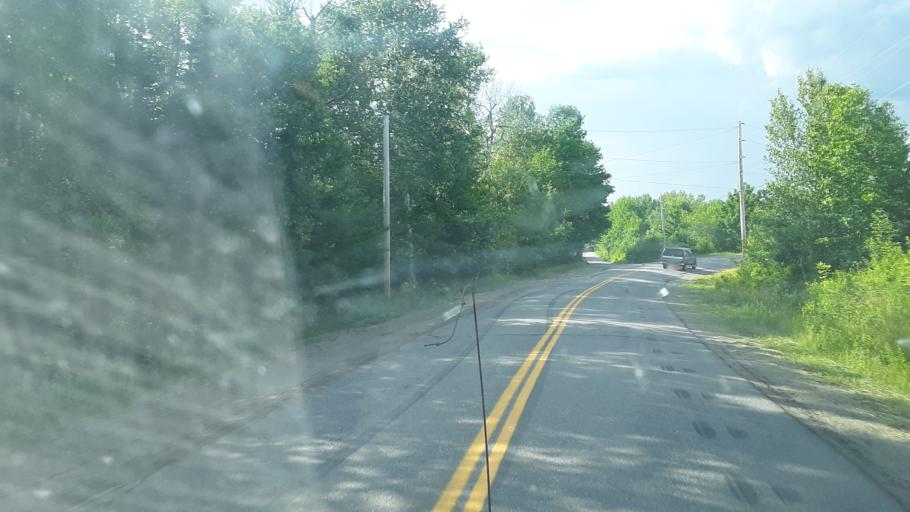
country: US
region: Maine
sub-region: Washington County
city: Calais
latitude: 45.1008
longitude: -67.5110
